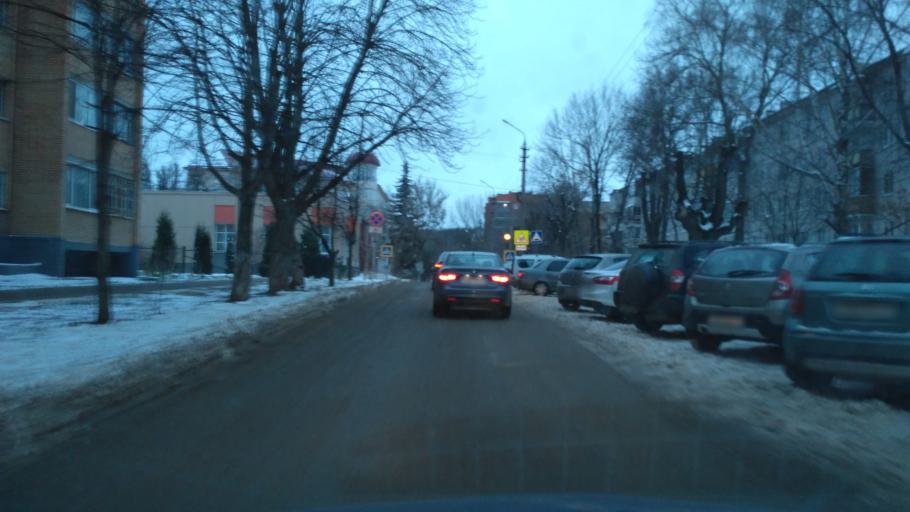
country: RU
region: Tula
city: Tula
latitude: 54.1875
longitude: 37.6011
